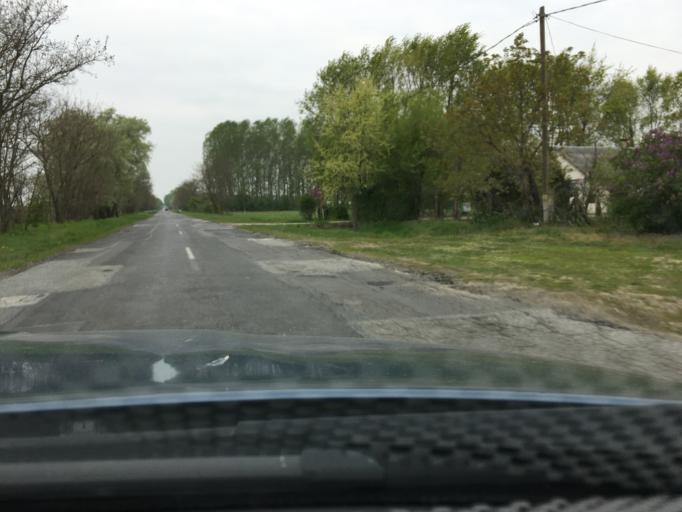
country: HU
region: Hajdu-Bihar
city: Debrecen
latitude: 47.5469
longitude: 21.6998
